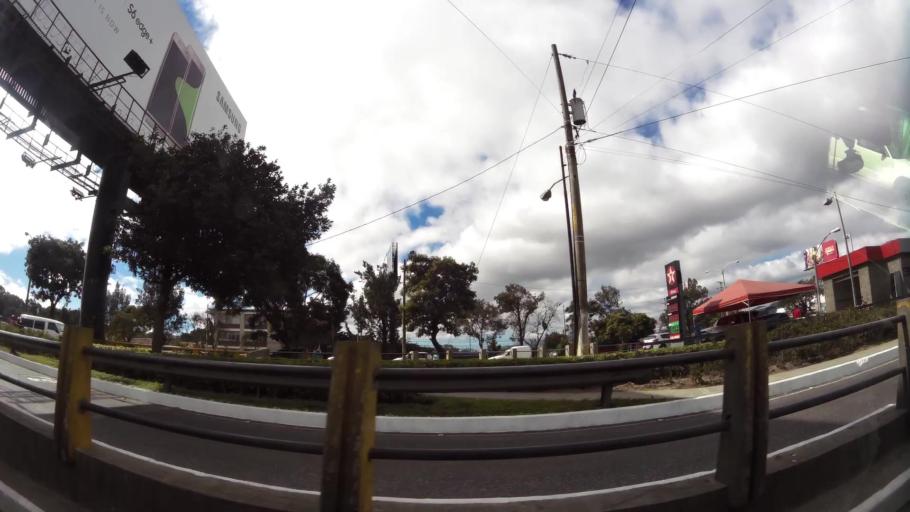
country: GT
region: Guatemala
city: Guatemala City
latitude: 14.6178
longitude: -90.5412
